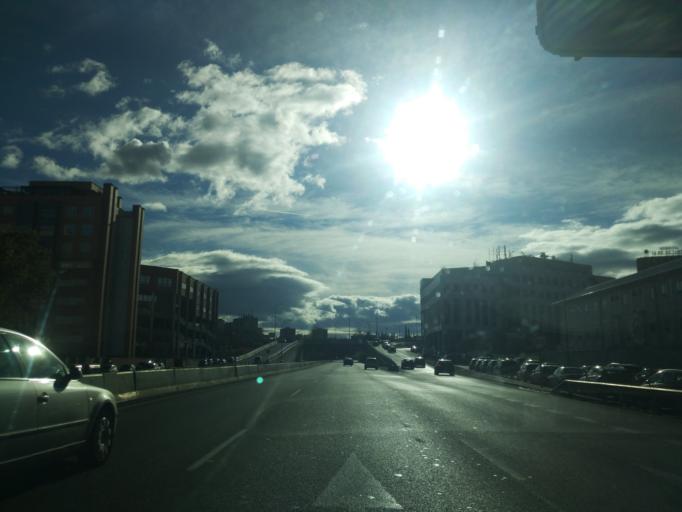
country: ES
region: Madrid
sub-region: Provincia de Madrid
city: Usera
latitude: 40.3783
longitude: -3.6931
